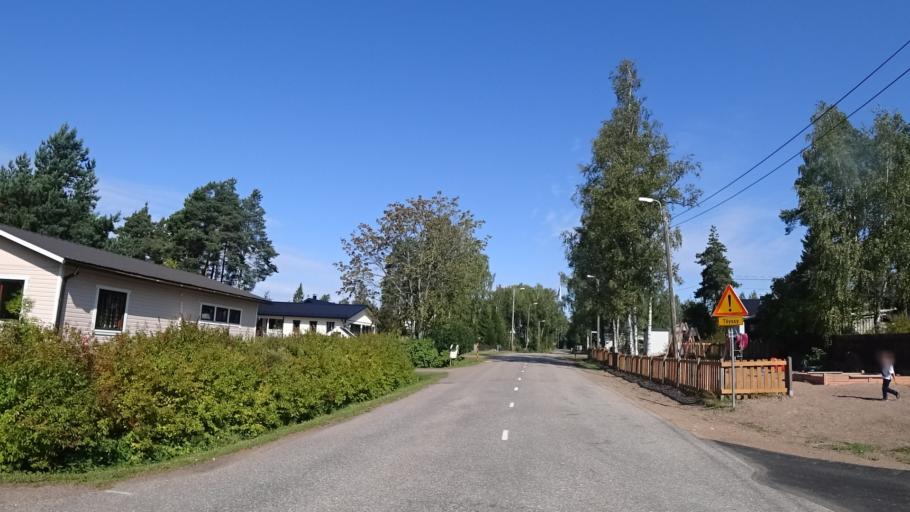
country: FI
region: Kymenlaakso
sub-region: Kotka-Hamina
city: Hamina
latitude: 60.5569
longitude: 27.1997
